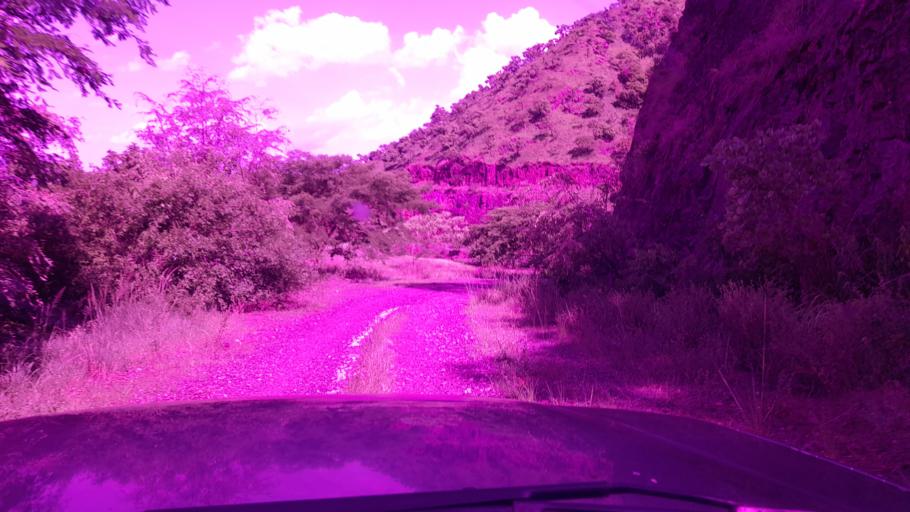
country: ET
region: Southern Nations, Nationalities, and People's Region
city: K'olito
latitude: 7.7744
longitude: 37.5539
